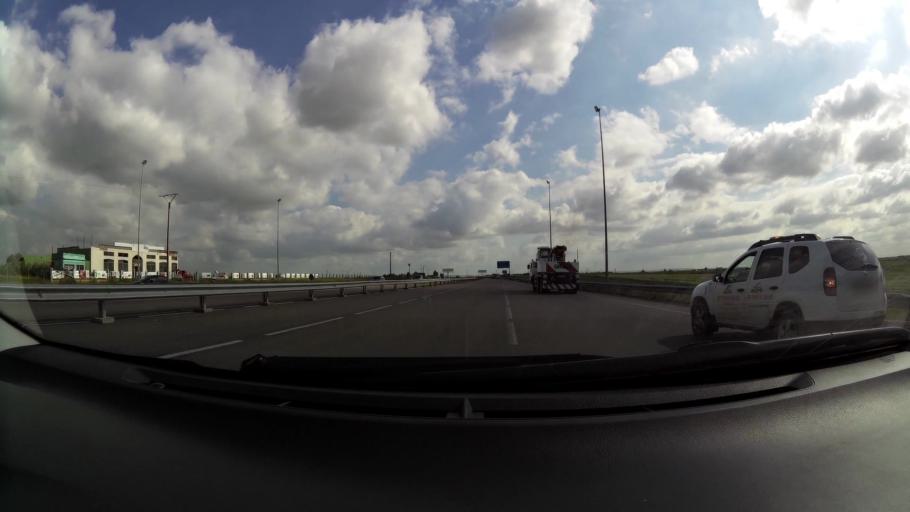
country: MA
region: Chaouia-Ouardigha
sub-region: Settat Province
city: Berrechid
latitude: 33.2290
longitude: -7.5734
